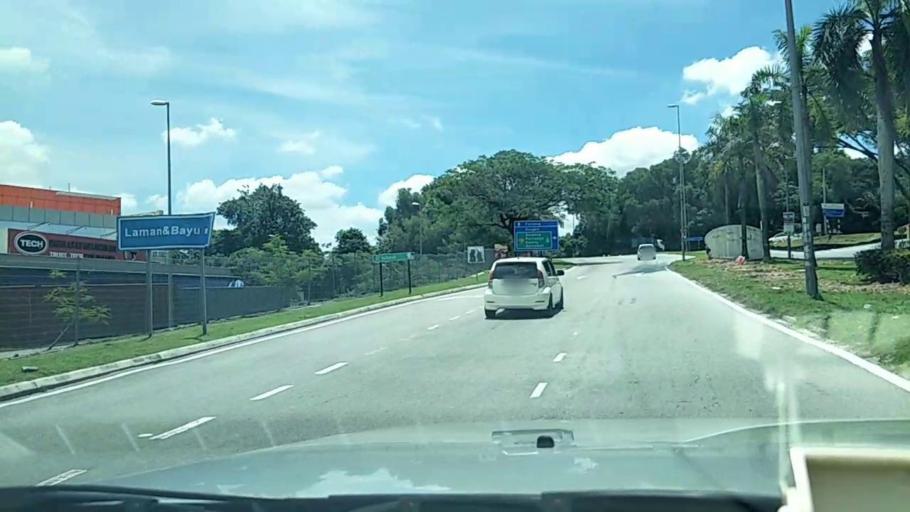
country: MY
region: Putrajaya
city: Putrajaya
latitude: 2.9620
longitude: 101.6176
